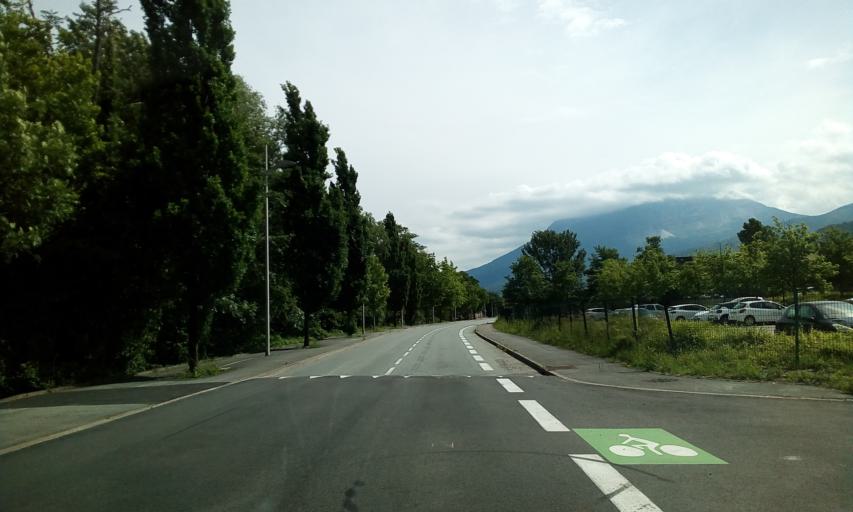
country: FR
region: Rhone-Alpes
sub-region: Departement de la Savoie
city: Saint-Baldoph
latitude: 45.5350
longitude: 5.9597
